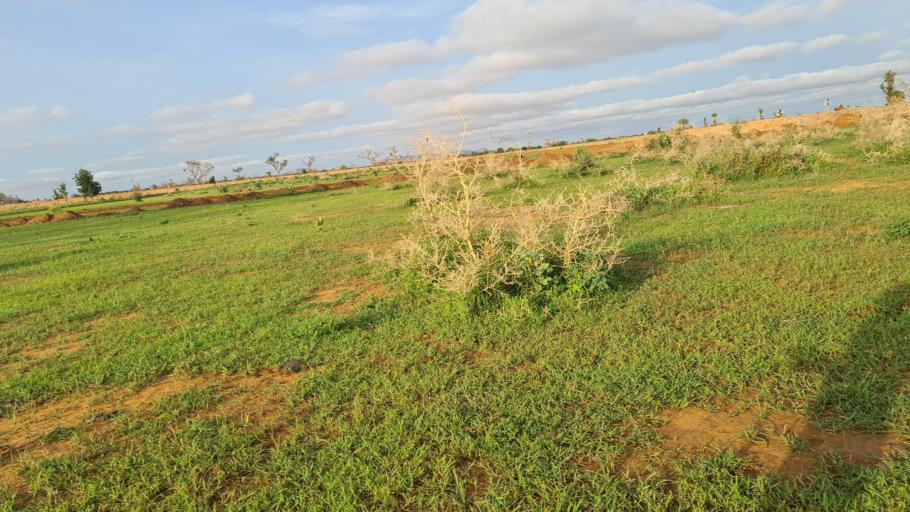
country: NE
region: Tahoua
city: Birni N Konni
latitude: 13.7858
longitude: 5.2311
